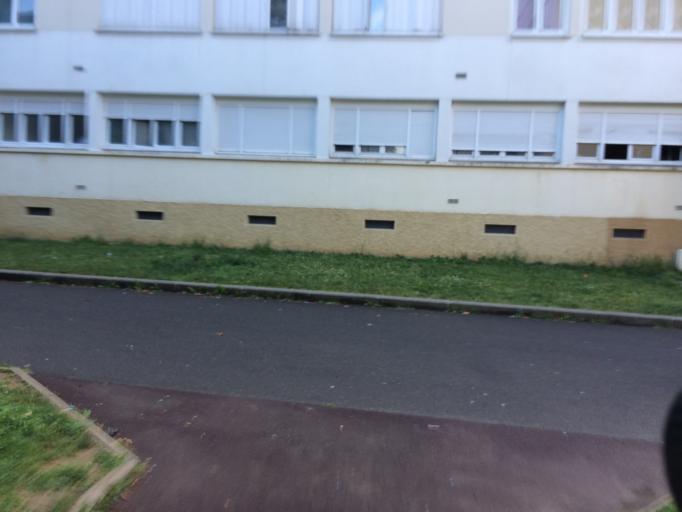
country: FR
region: Ile-de-France
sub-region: Departement de l'Essonne
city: Massy
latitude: 48.7364
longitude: 2.2869
